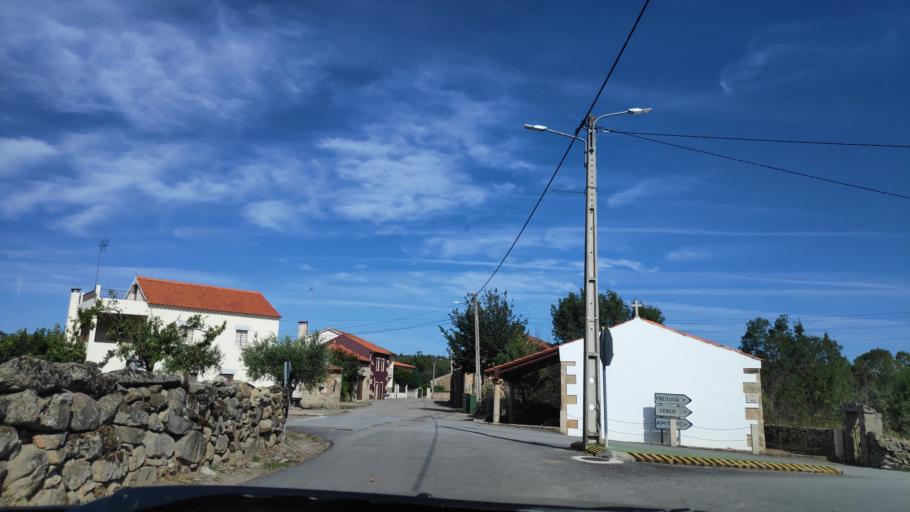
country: ES
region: Castille and Leon
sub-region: Provincia de Zamora
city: Fariza
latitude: 41.4296
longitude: -6.3458
